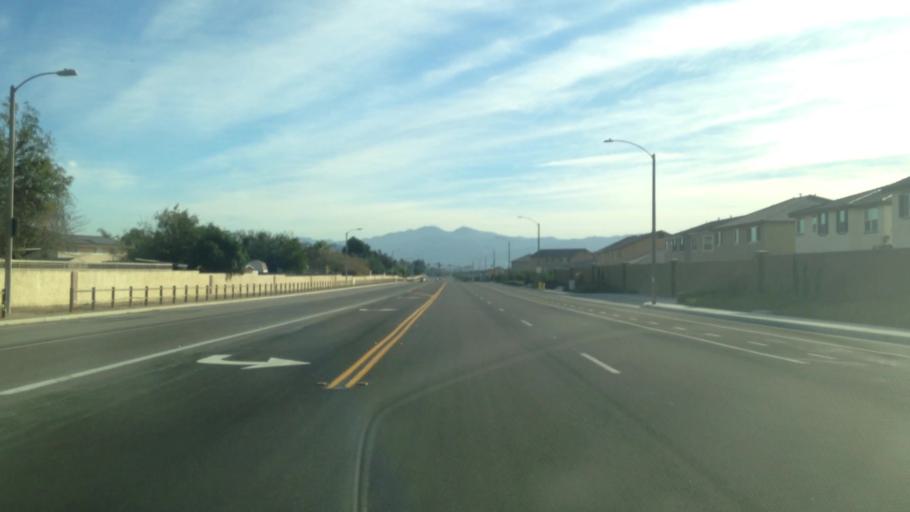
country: US
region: California
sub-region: Riverside County
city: Mira Loma
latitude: 33.9891
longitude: -117.5407
